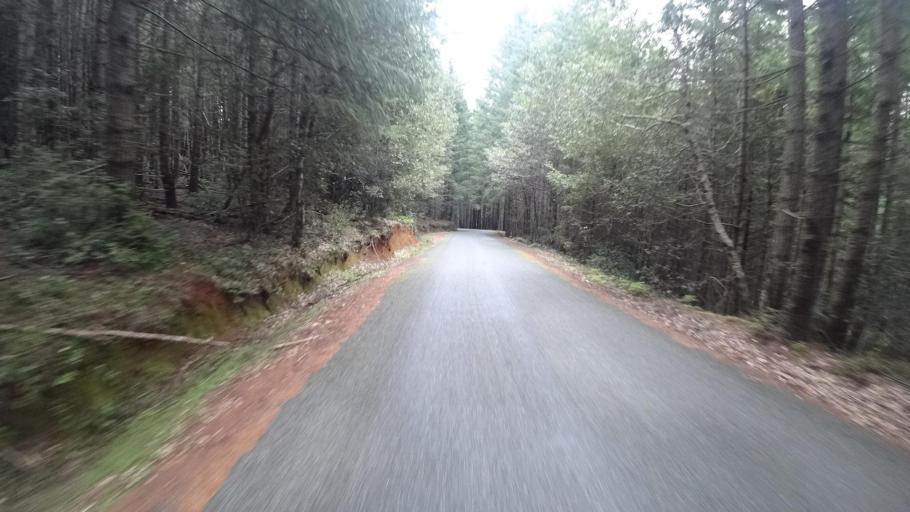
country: US
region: California
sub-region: Humboldt County
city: Willow Creek
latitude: 41.1998
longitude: -123.7758
